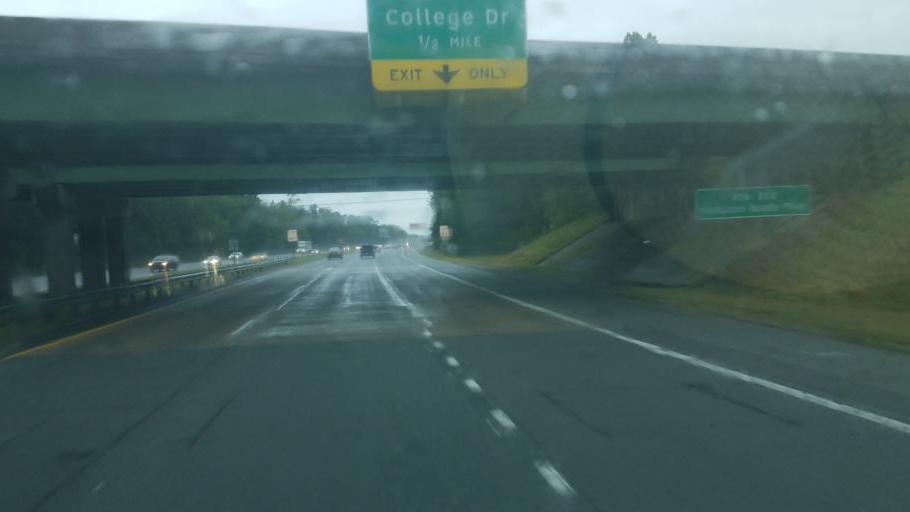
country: US
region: Virginia
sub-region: City of Portsmouth
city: Portsmouth Heights
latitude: 36.8760
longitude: -76.4332
